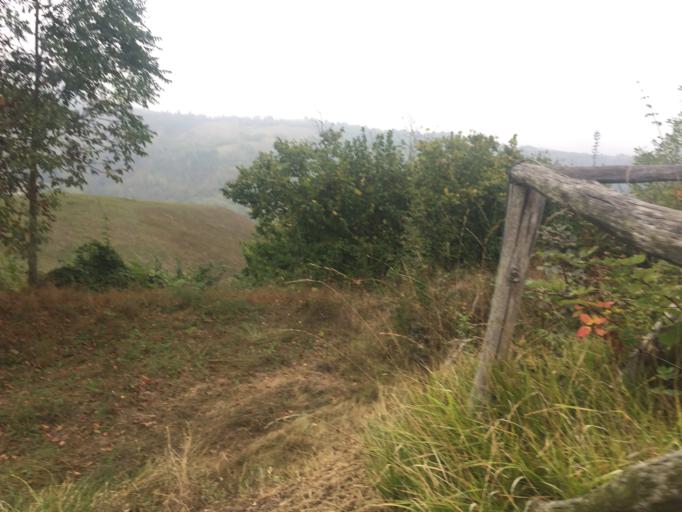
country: IT
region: Piedmont
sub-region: Provincia di Cuneo
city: Paroldo
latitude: 44.4339
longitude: 8.0752
